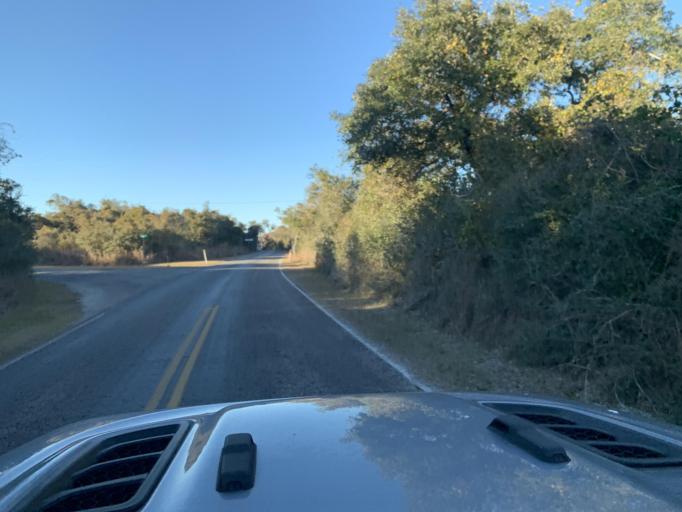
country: US
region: Texas
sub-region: Aransas County
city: Fulton
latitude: 28.1405
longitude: -96.9842
